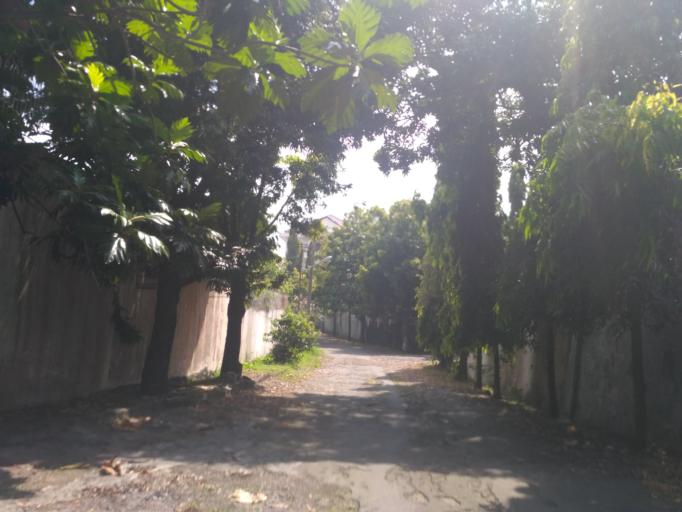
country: ID
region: Central Java
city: Semarang
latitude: -7.0419
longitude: 110.4275
